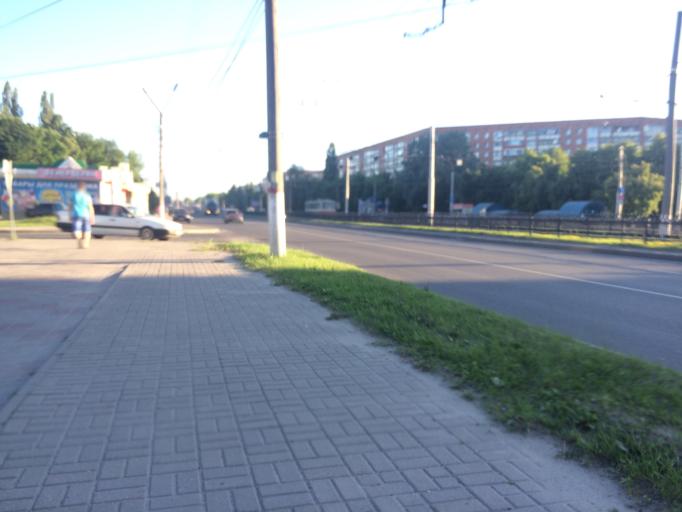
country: RU
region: Kursk
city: Kursk
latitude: 51.6721
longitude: 36.1436
